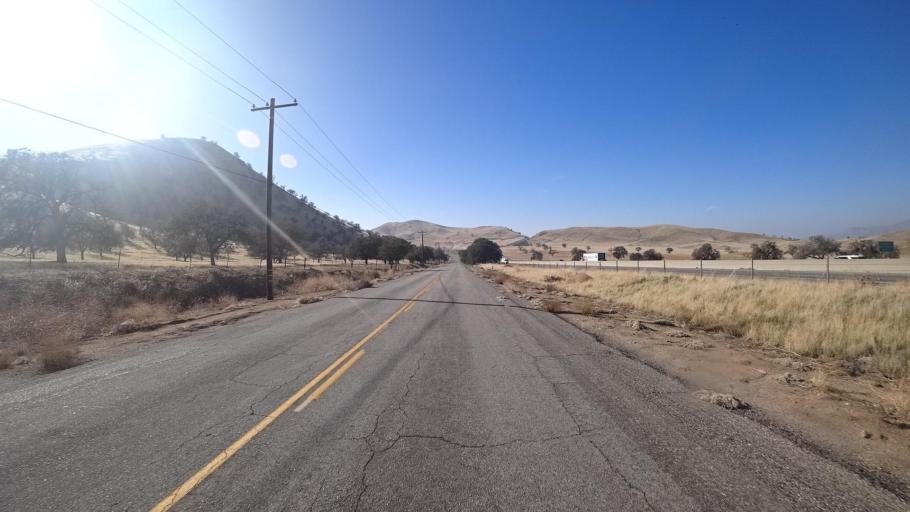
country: US
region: California
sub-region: Kern County
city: Bear Valley Springs
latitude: 35.2636
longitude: -118.6501
